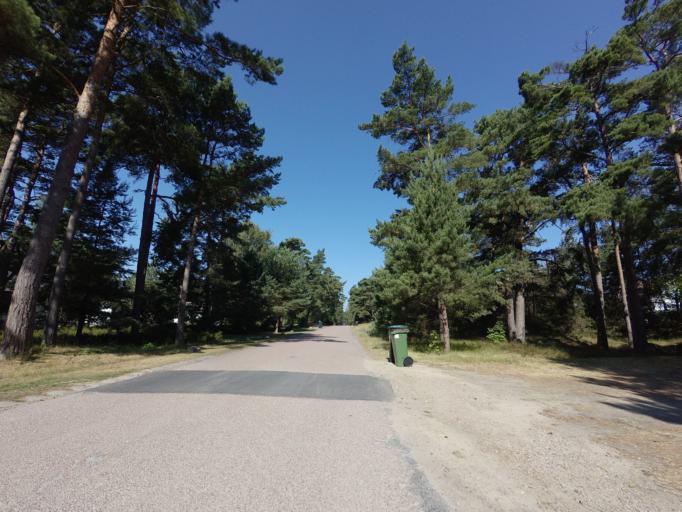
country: SE
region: Skane
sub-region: Vellinge Kommun
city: Ljunghusen
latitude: 55.3922
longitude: 12.9287
